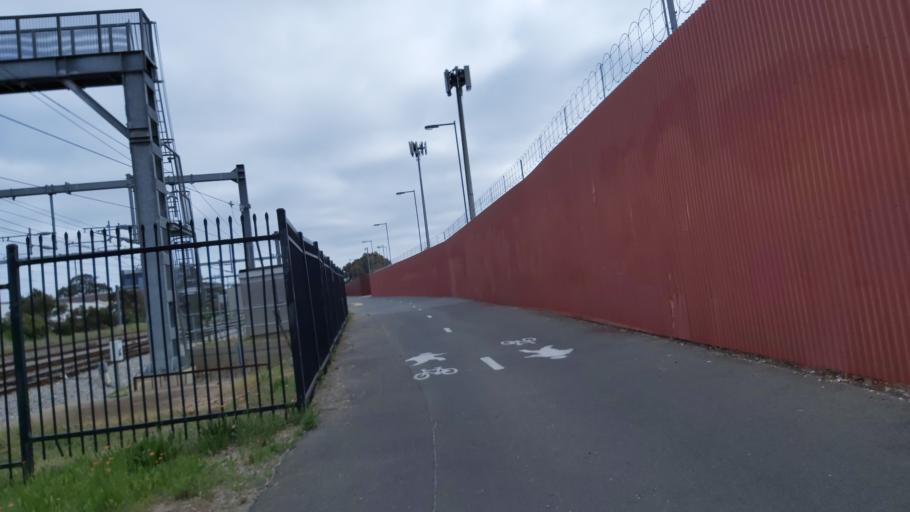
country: AU
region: South Australia
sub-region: Unley
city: Wayville
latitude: -34.9465
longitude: 138.5840
